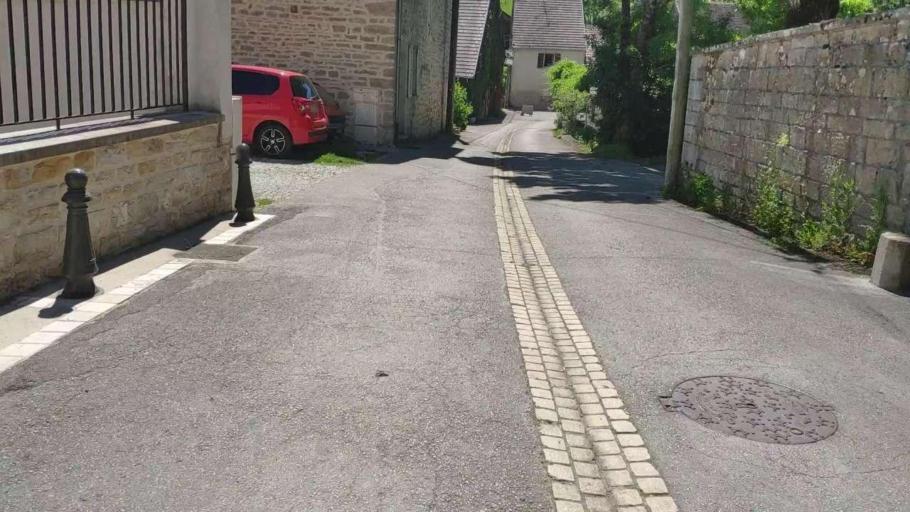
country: FR
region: Franche-Comte
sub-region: Departement du Jura
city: Perrigny
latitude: 46.7422
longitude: 5.6308
